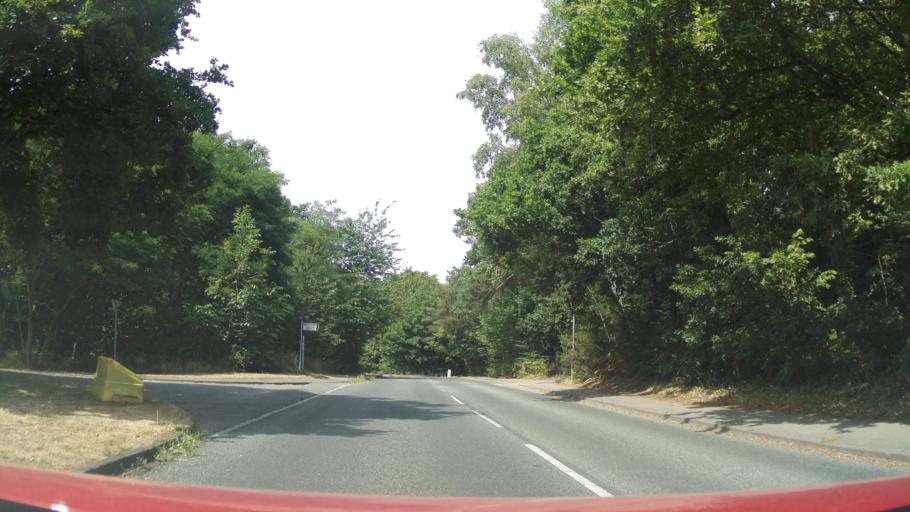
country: GB
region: England
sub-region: Surrey
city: Pirbright
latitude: 51.3053
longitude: -0.6506
